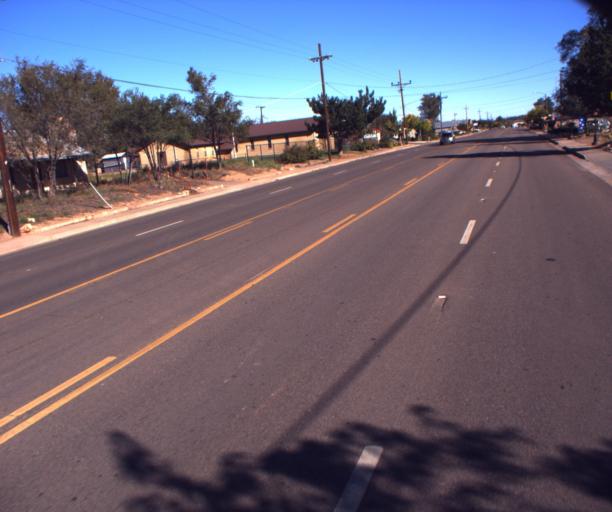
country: US
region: Arizona
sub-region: Navajo County
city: Taylor
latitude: 34.4626
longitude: -110.0911
